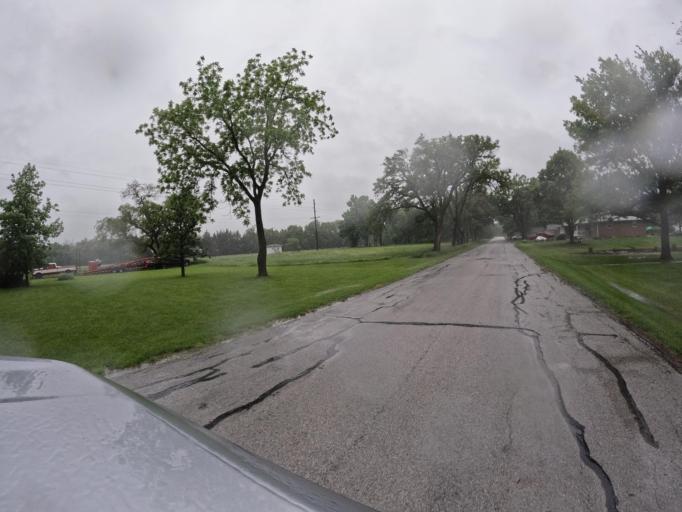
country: US
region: Nebraska
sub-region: Gage County
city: Wymore
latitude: 40.1386
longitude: -96.6673
